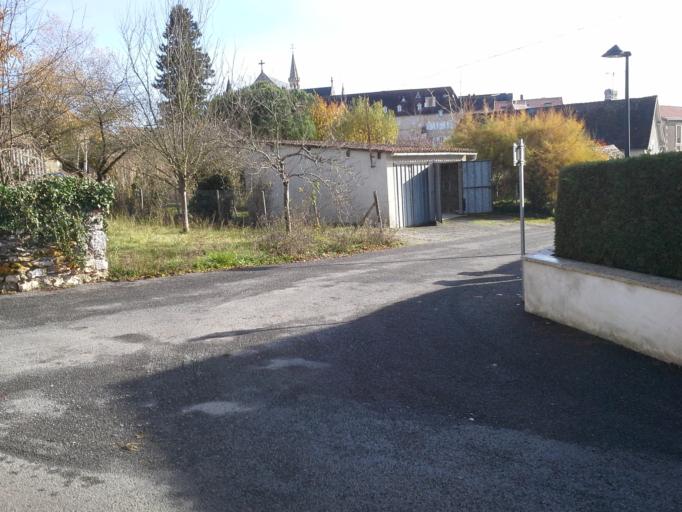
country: FR
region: Poitou-Charentes
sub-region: Departement de la Vienne
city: Pleumartin
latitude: 46.6417
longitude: 0.7510
